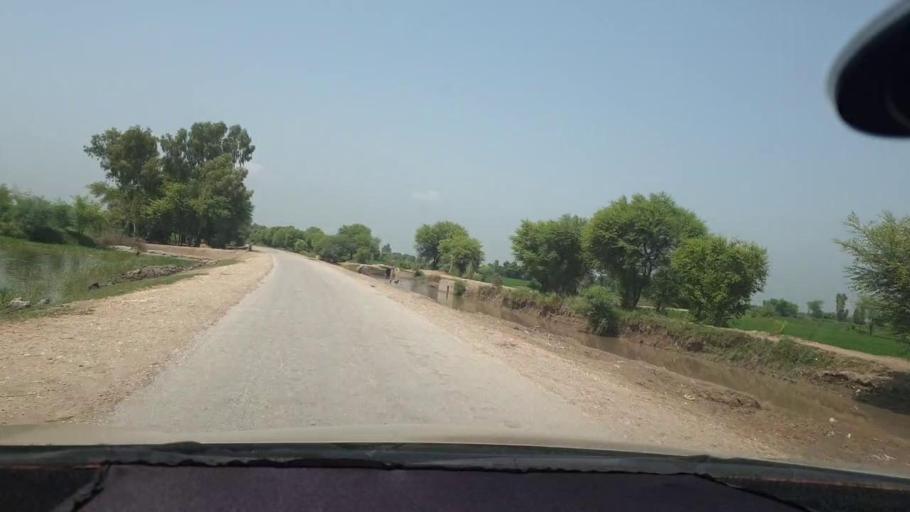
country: PK
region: Sindh
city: Kambar
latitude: 27.6584
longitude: 67.9559
